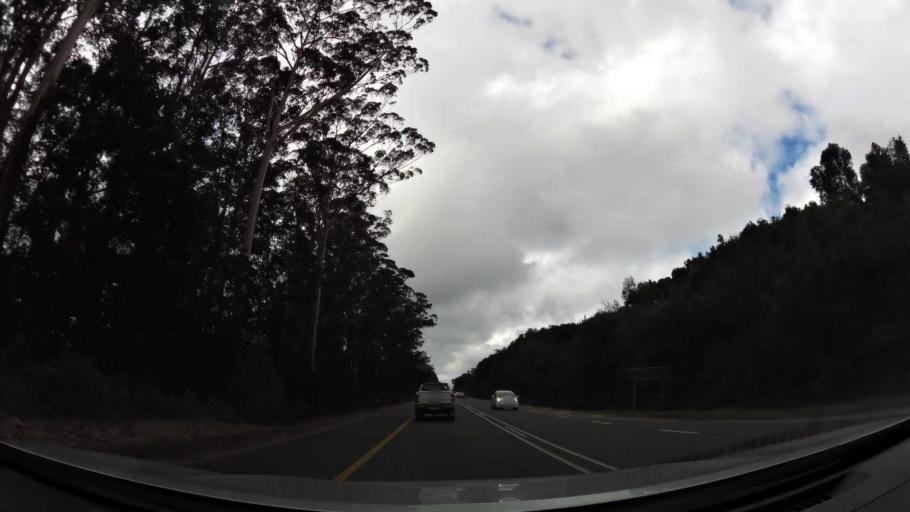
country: ZA
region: Western Cape
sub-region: Eden District Municipality
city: Plettenberg Bay
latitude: -34.0375
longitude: 23.2170
